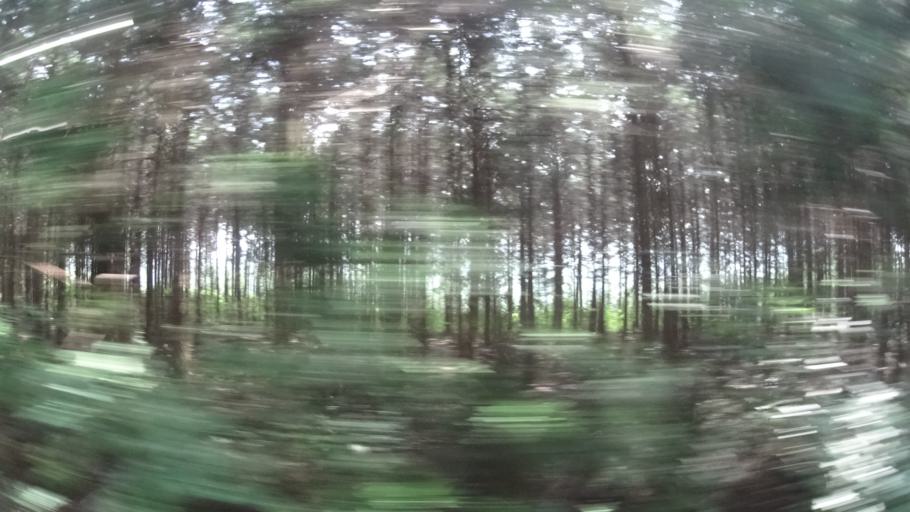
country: JP
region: Tochigi
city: Kanuma
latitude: 36.6203
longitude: 139.7352
